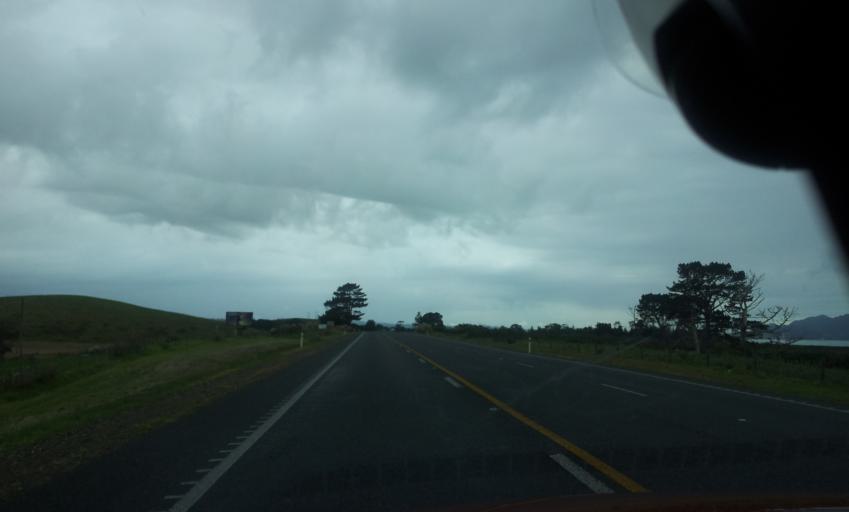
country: NZ
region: Northland
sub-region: Whangarei
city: Ruakaka
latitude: -35.9272
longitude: 174.4542
